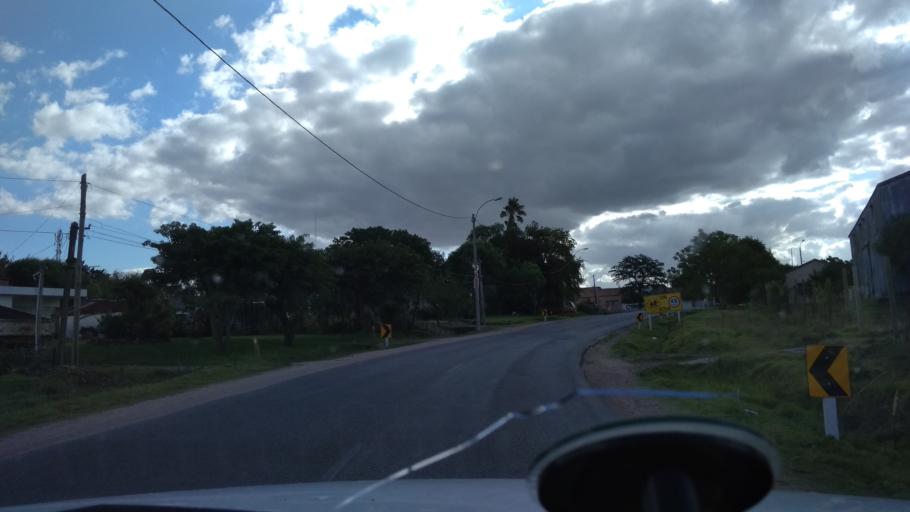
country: UY
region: Canelones
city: Tala
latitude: -34.3424
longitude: -55.7567
